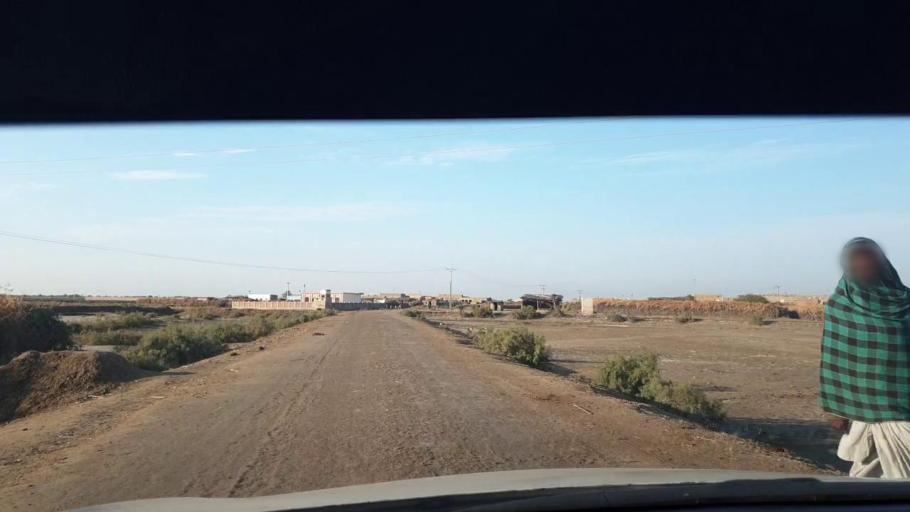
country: PK
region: Sindh
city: Berani
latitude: 25.8080
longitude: 68.9024
